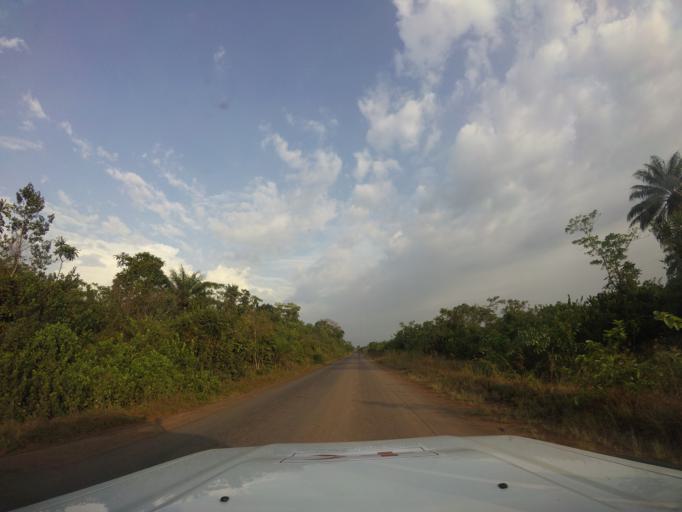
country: LR
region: Bomi
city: Tubmanburg
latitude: 6.7293
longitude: -10.9895
